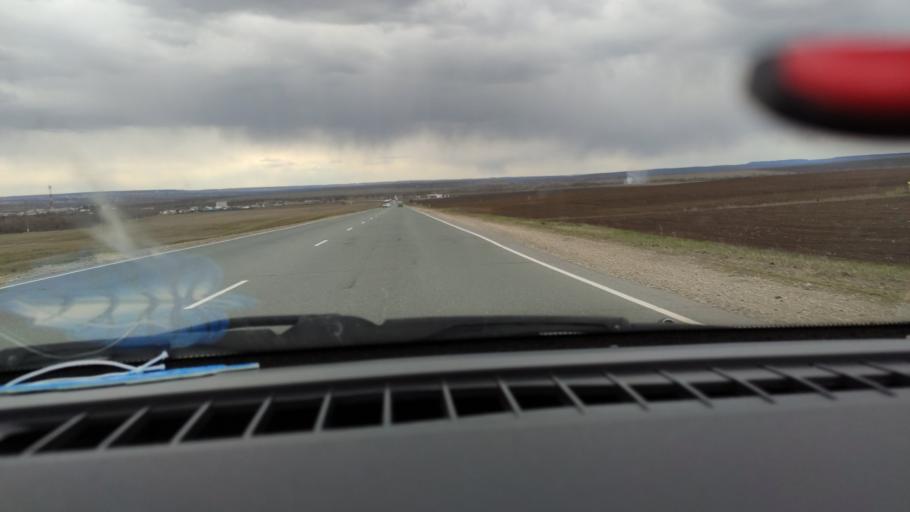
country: RU
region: Saratov
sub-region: Saratovskiy Rayon
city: Saratov
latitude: 51.7402
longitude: 46.0438
